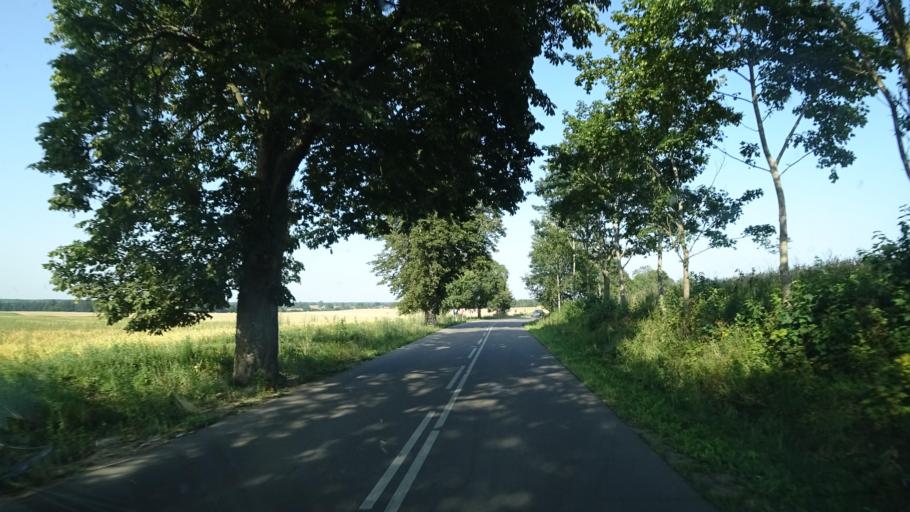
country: PL
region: Pomeranian Voivodeship
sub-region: Powiat czluchowski
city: Przechlewo
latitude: 53.8042
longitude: 17.2769
